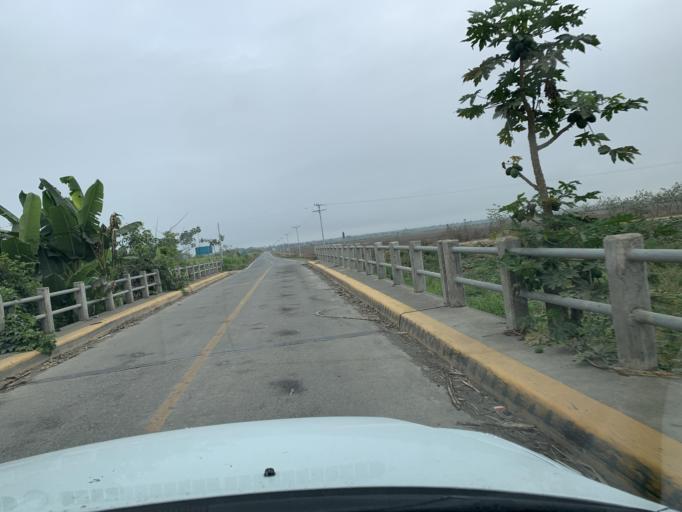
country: EC
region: Guayas
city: Coronel Marcelino Mariduena
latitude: -2.3050
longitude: -79.5017
